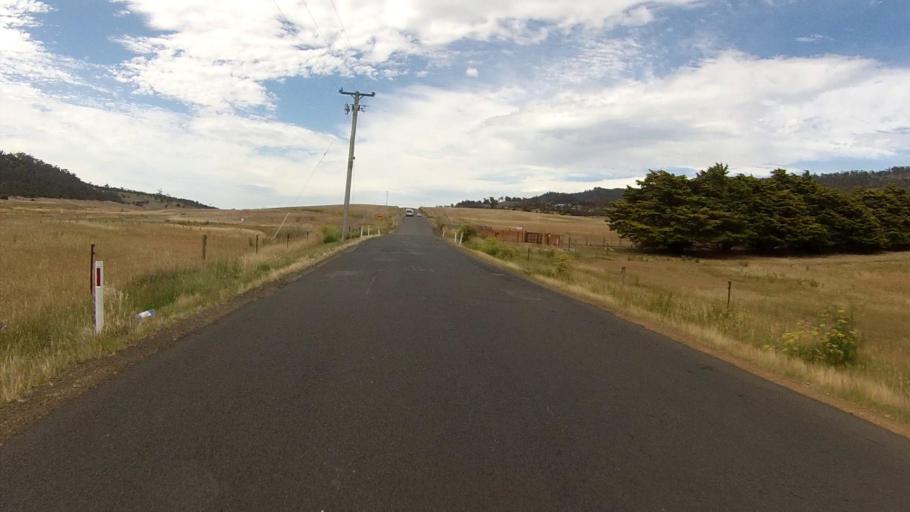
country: AU
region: Tasmania
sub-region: Brighton
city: Old Beach
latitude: -42.7302
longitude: 147.3475
